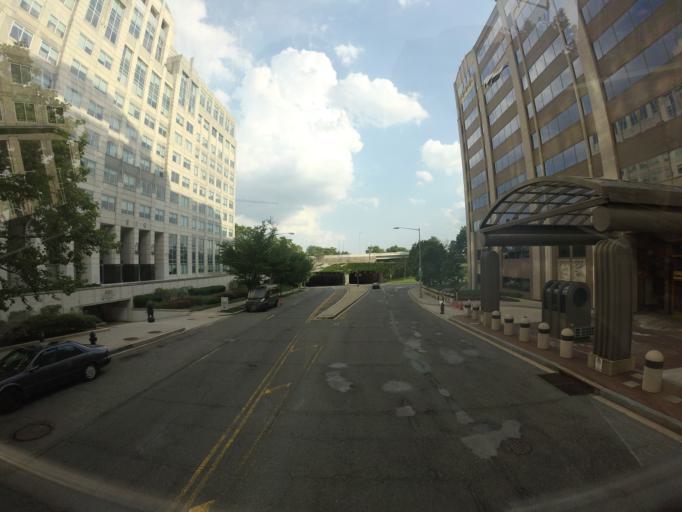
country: US
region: Washington, D.C.
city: Washington, D.C.
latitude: 38.8835
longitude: -77.0281
